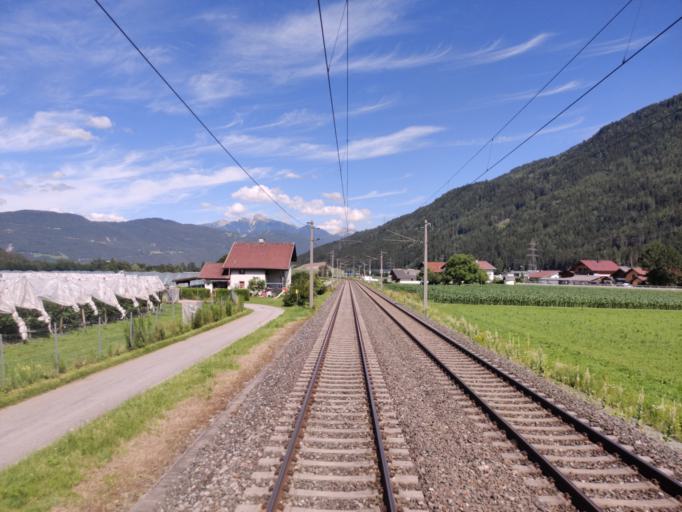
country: AT
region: Tyrol
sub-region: Politischer Bezirk Imst
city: Rietz
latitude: 47.2927
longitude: 11.0378
